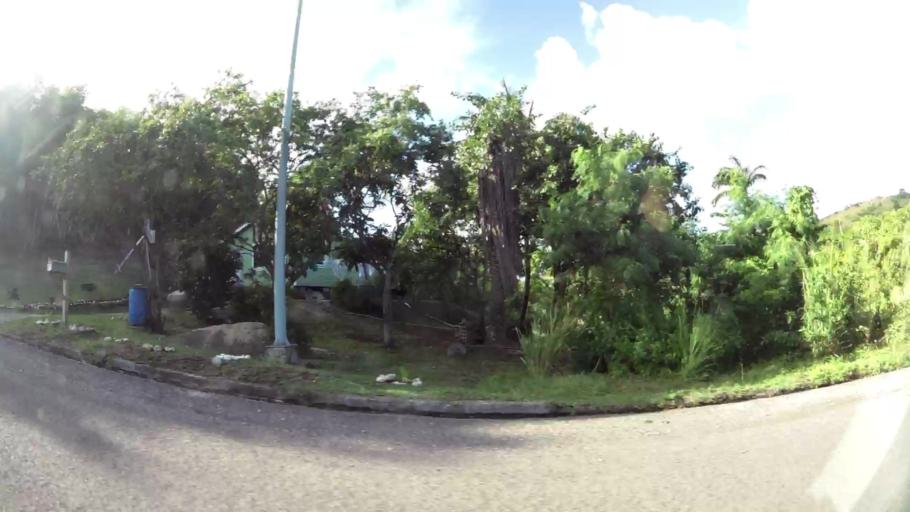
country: AG
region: Saint Peter
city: All Saints
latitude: 17.0463
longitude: -61.8139
